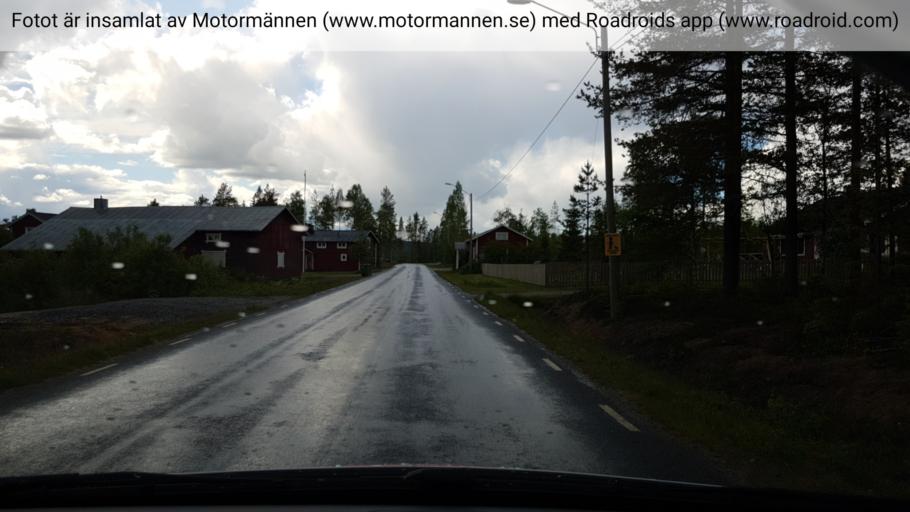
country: SE
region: Vaesterbotten
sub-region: Umea Kommun
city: Roback
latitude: 63.9950
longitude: 20.1073
